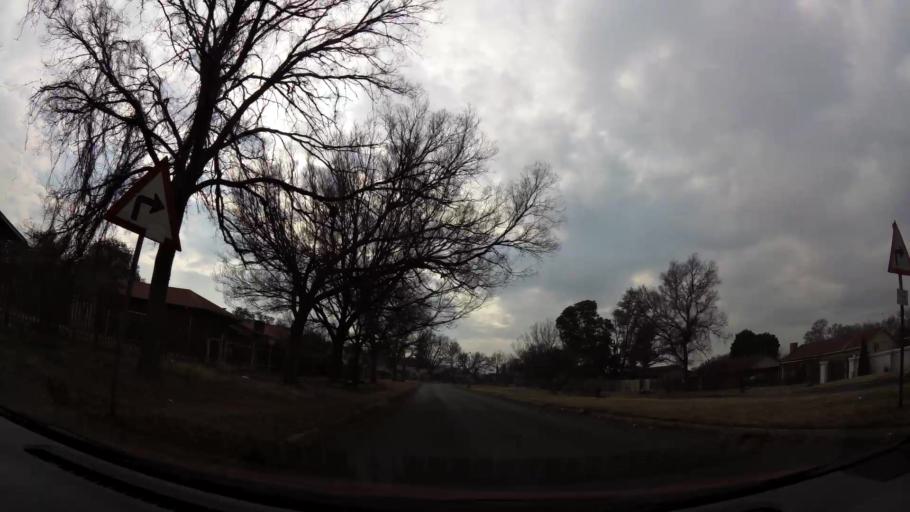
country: ZA
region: Gauteng
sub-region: Sedibeng District Municipality
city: Vanderbijlpark
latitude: -26.6851
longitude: 27.8296
